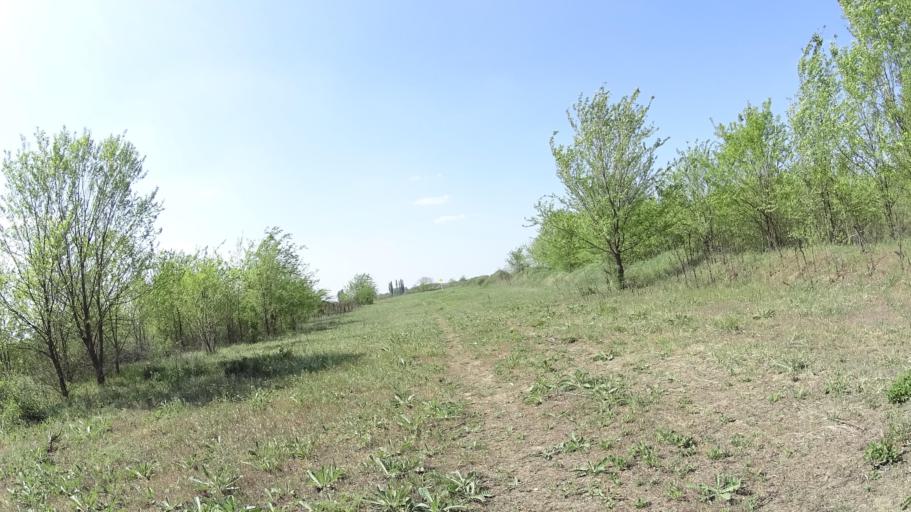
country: HU
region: Pest
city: Vecses
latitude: 47.4255
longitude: 19.3042
